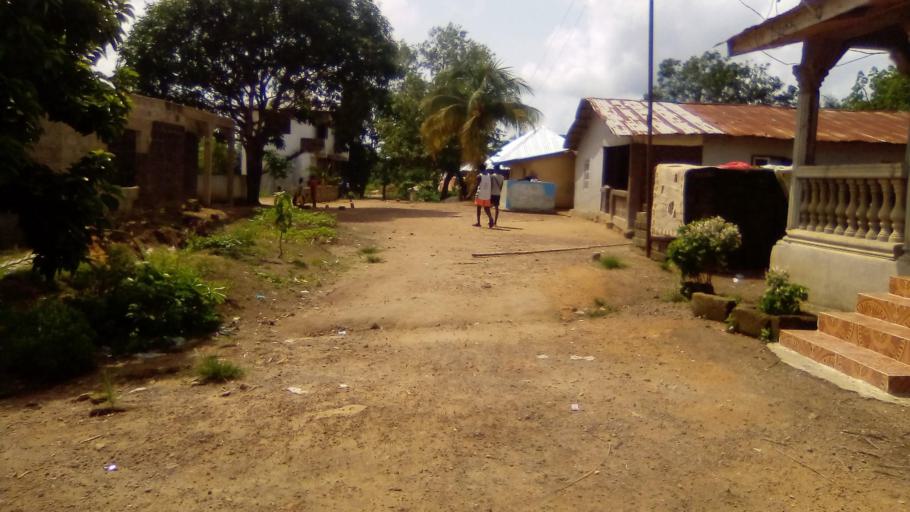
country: SL
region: Southern Province
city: Bo
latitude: 7.9788
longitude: -11.7435
